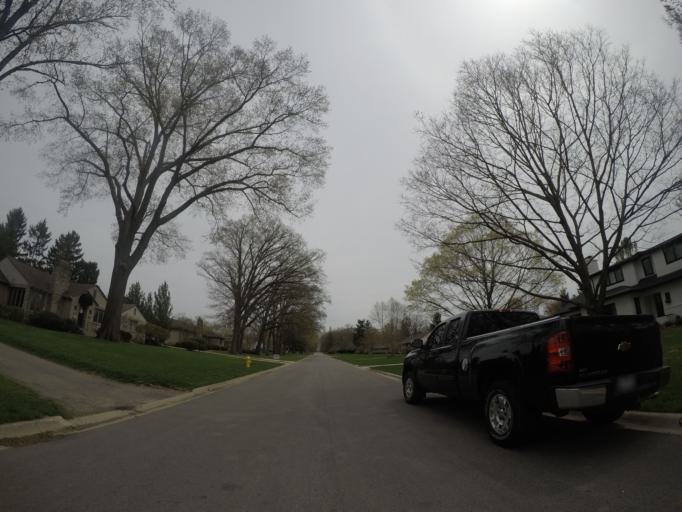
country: US
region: Ohio
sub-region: Franklin County
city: Upper Arlington
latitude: 40.0148
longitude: -83.0811
